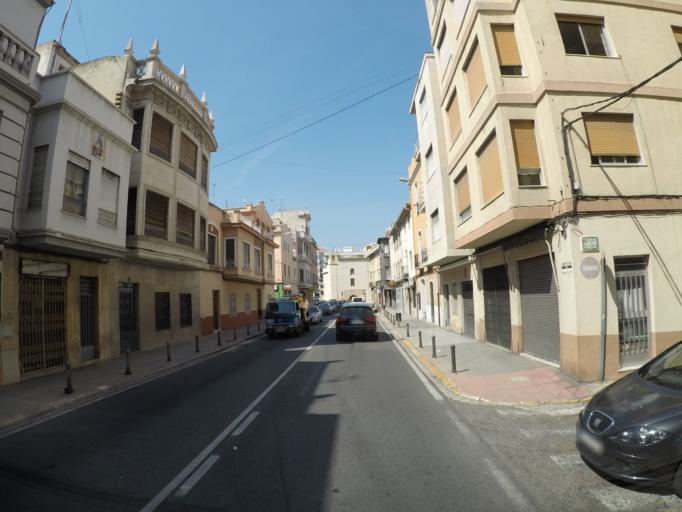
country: ES
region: Valencia
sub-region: Provincia de Valencia
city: Oliva
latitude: 38.9209
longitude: -0.1185
